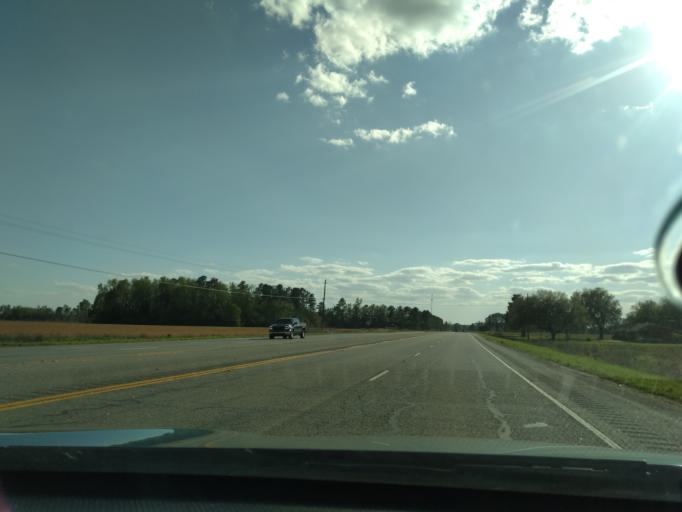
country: US
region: South Carolina
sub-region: Williamsburg County
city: Kingstree
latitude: 33.6483
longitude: -79.8880
